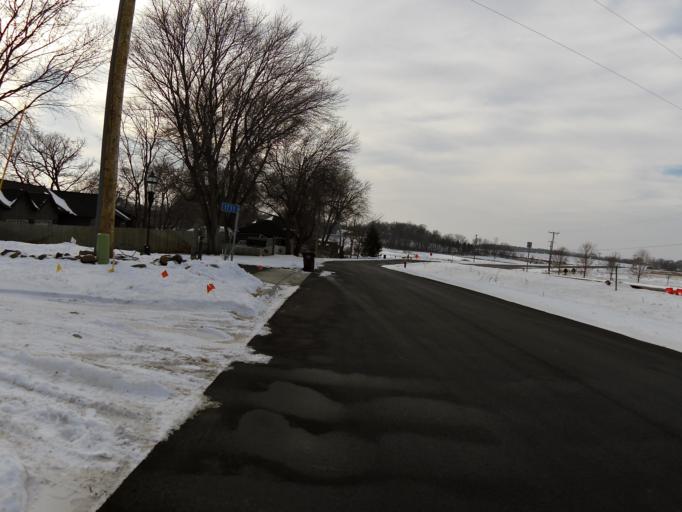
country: US
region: Minnesota
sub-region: Scott County
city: Prior Lake
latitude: 44.7044
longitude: -93.4858
